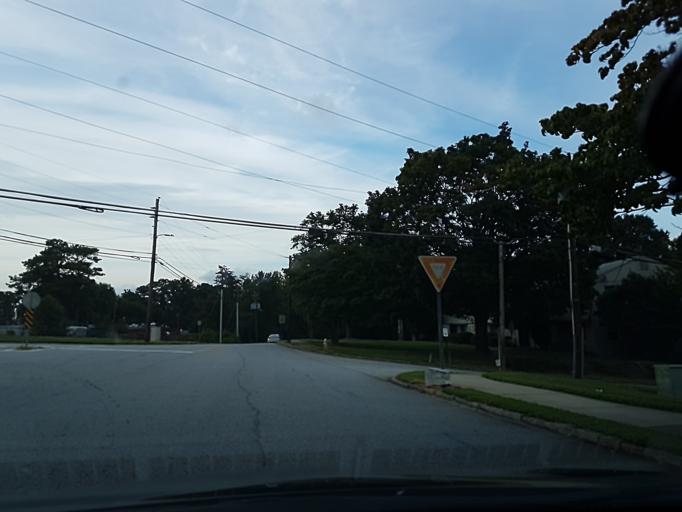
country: US
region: Georgia
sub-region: DeKalb County
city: North Decatur
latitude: 33.7912
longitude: -84.3044
